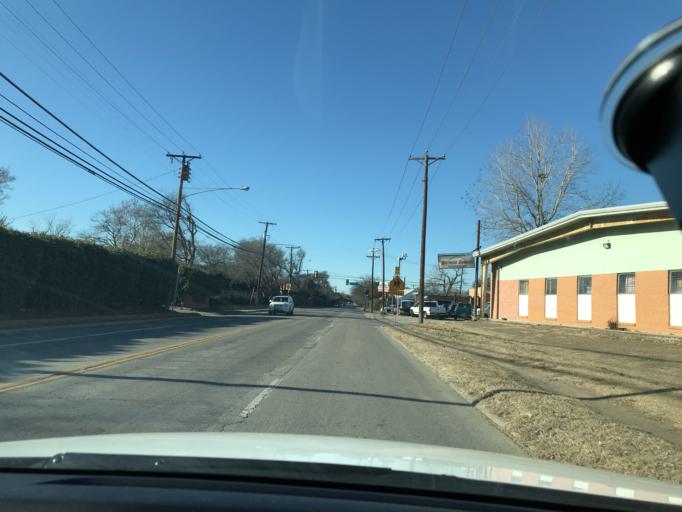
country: US
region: Texas
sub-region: Dallas County
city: Garland
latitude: 32.8334
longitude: -96.6906
